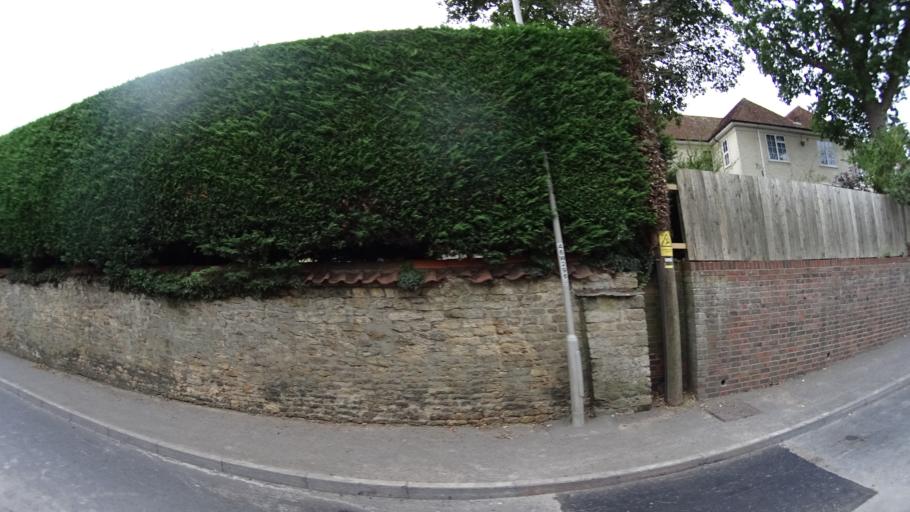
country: GB
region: England
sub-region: Dorset
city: Gillingham
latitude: 51.0380
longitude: -2.2827
